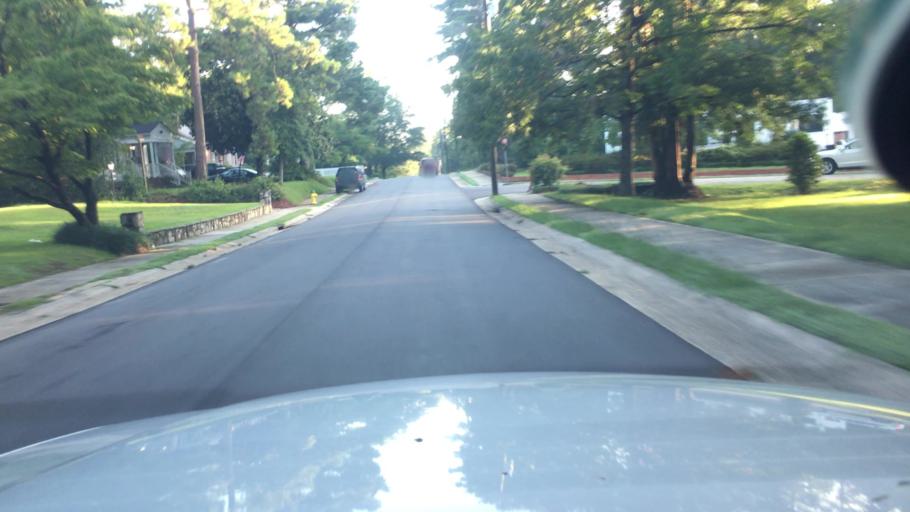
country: US
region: North Carolina
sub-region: Cumberland County
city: Fayetteville
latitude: 35.0632
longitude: -78.9074
